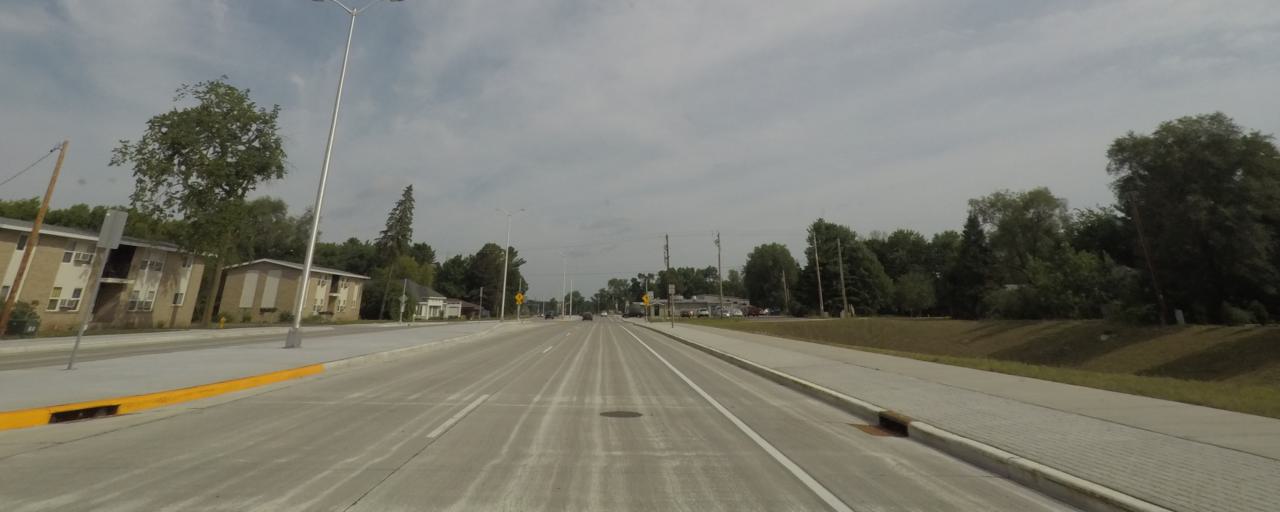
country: US
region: Wisconsin
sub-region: Portage County
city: Whiting
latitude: 44.4890
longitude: -89.5512
